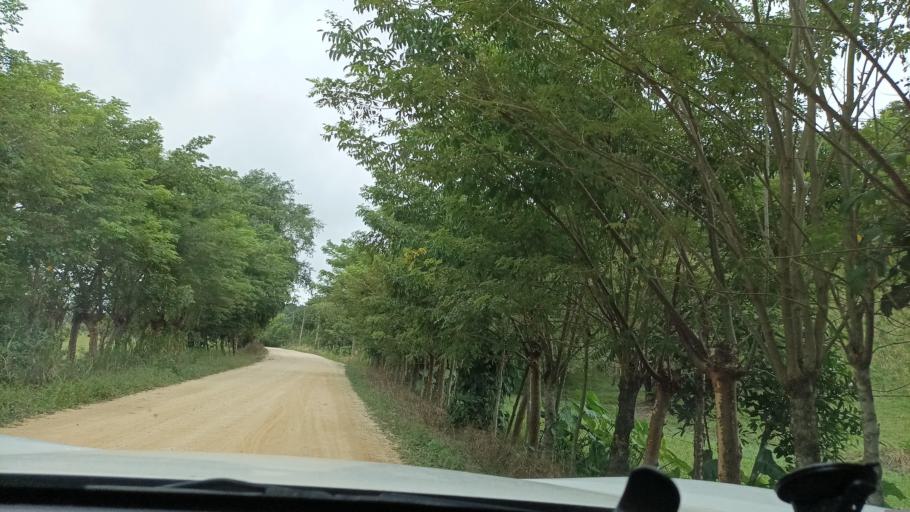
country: MX
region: Veracruz
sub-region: Moloacan
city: Cuichapa
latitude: 17.8347
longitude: -94.3528
